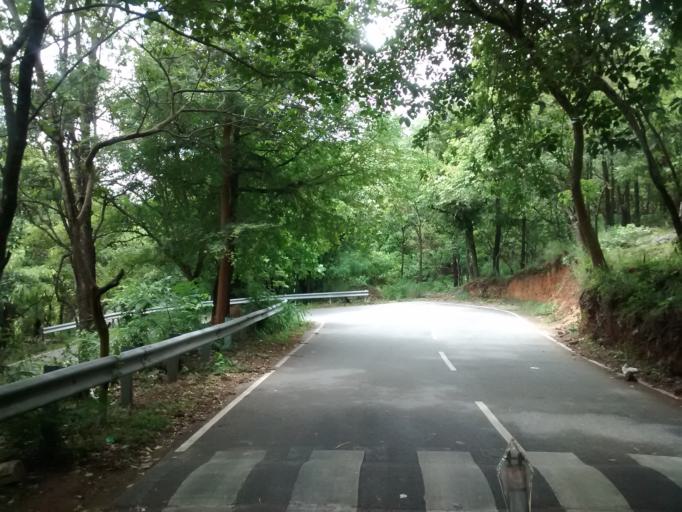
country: IN
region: Andhra Pradesh
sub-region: Chittoor
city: Tirumala
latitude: 13.6809
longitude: 79.3321
